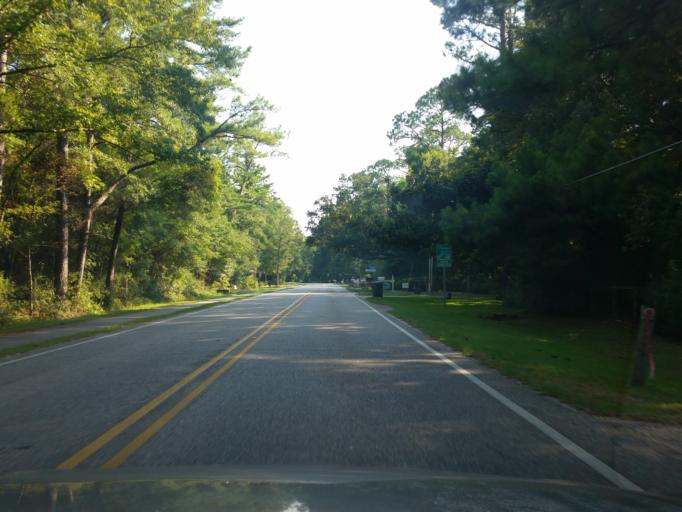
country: US
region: Alabama
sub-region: Baldwin County
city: Fairhope
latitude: 30.5064
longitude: -87.9205
